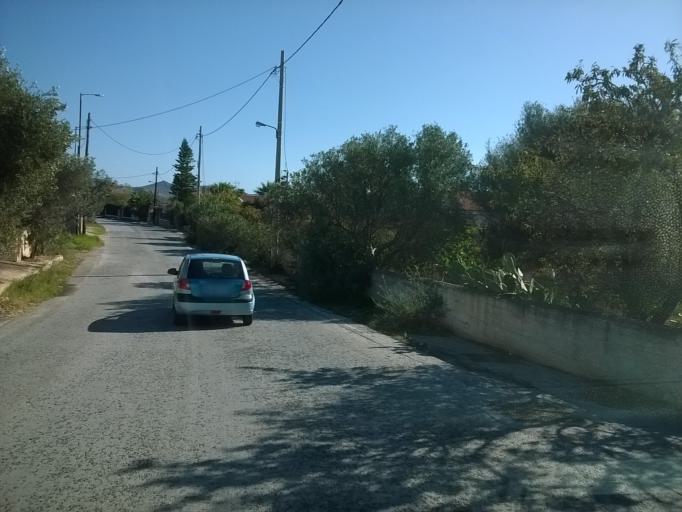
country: GR
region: Attica
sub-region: Nomarchia Anatolikis Attikis
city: Anavyssos
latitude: 37.7361
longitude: 23.9309
